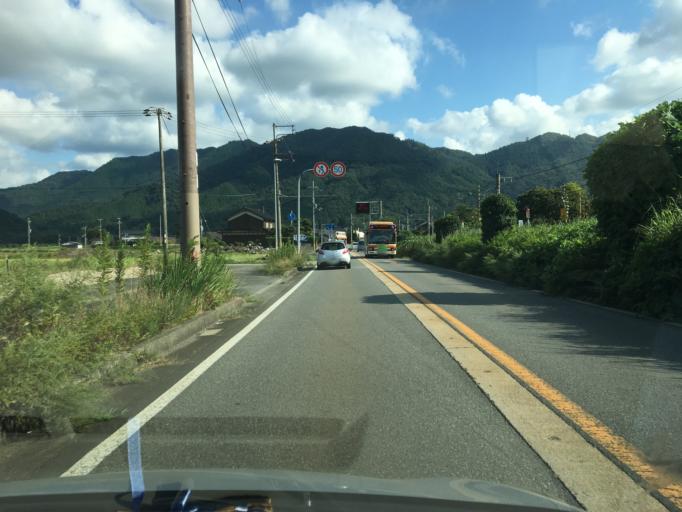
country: JP
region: Hyogo
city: Toyooka
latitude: 35.4266
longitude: 134.7885
